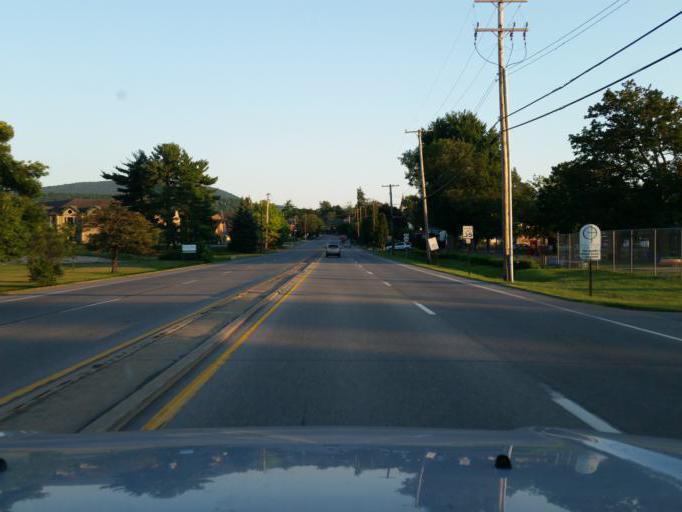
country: US
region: Pennsylvania
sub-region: Blair County
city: Hollidaysburg
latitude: 40.4390
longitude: -78.3925
